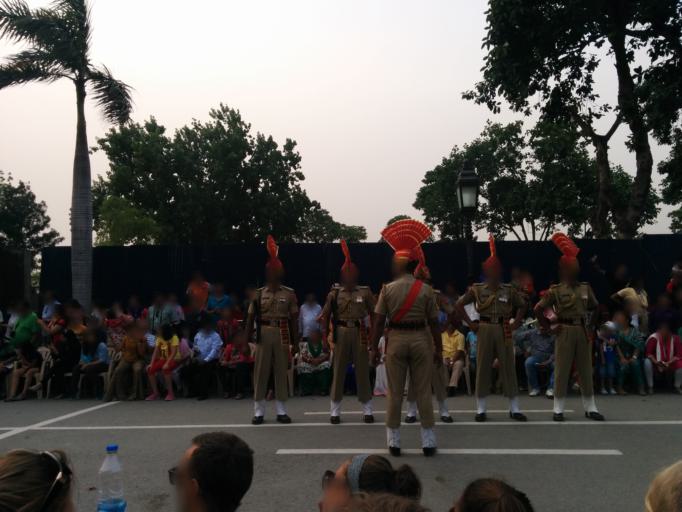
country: PK
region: Punjab
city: Lahore
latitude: 31.6047
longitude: 74.5735
